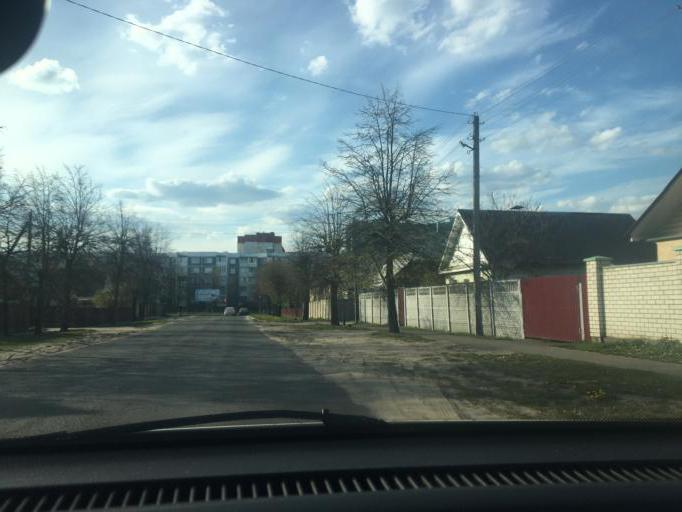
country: BY
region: Mogilev
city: Babruysk
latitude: 53.1563
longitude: 29.1934
